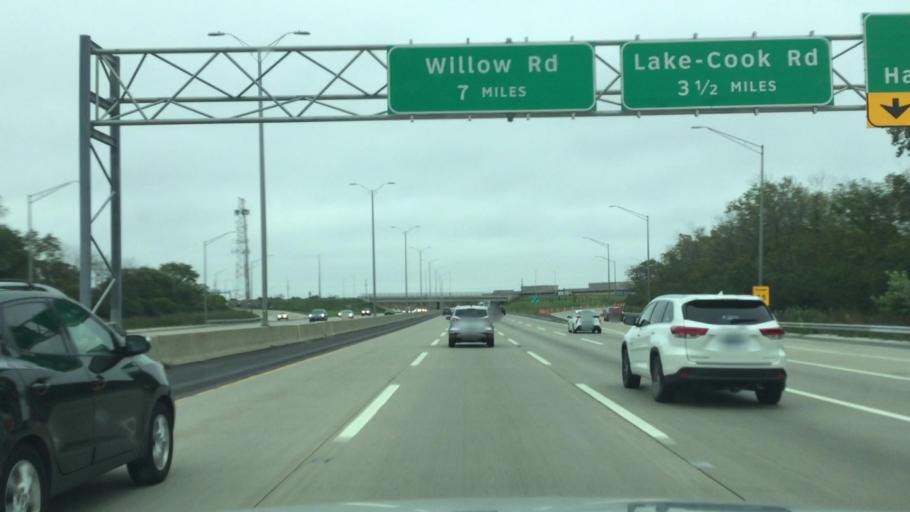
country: US
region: Illinois
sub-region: Lake County
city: Lincolnshire
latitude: 42.2046
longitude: -87.8909
